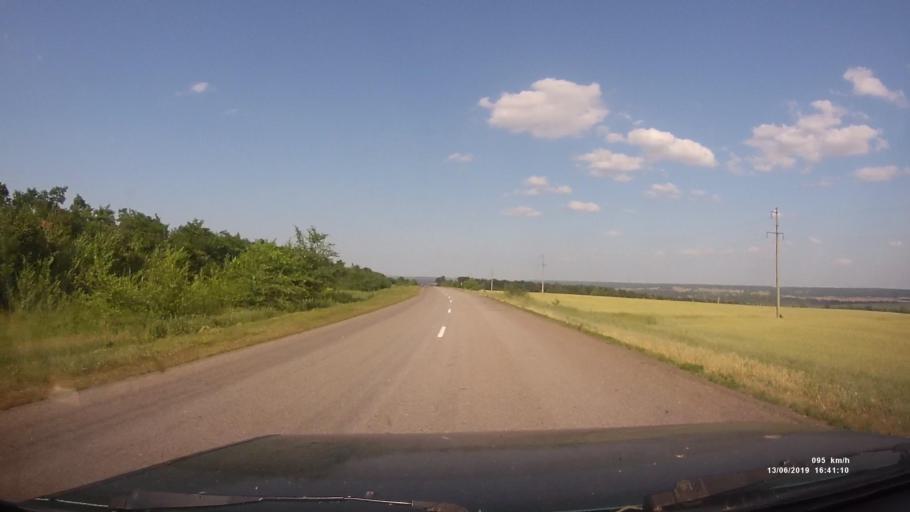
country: RU
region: Rostov
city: Kazanskaya
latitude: 49.9343
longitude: 41.3780
